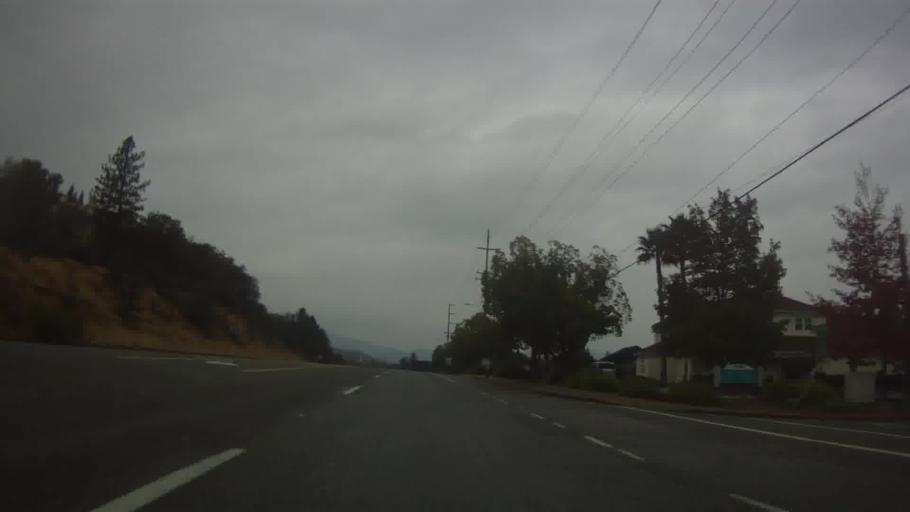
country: US
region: California
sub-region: Shasta County
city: Redding
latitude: 40.5855
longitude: -122.4166
